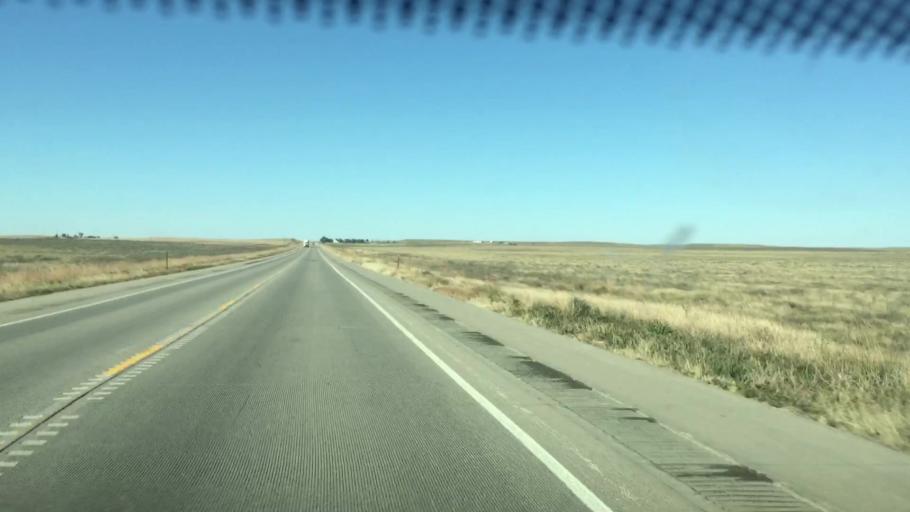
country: US
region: Colorado
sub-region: Kiowa County
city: Eads
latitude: 38.7109
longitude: -102.7759
